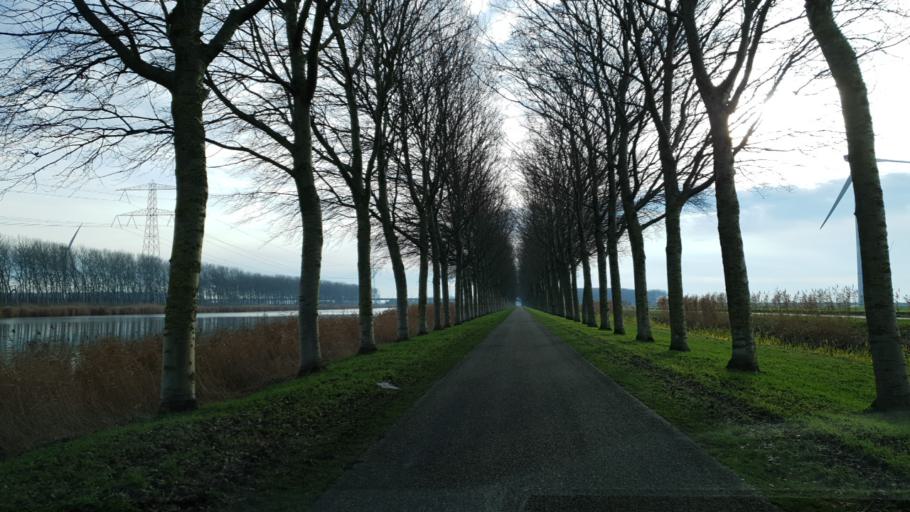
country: NL
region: North Brabant
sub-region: Gemeente Woensdrecht
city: Woensdrecht
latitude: 51.4115
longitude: 4.2328
